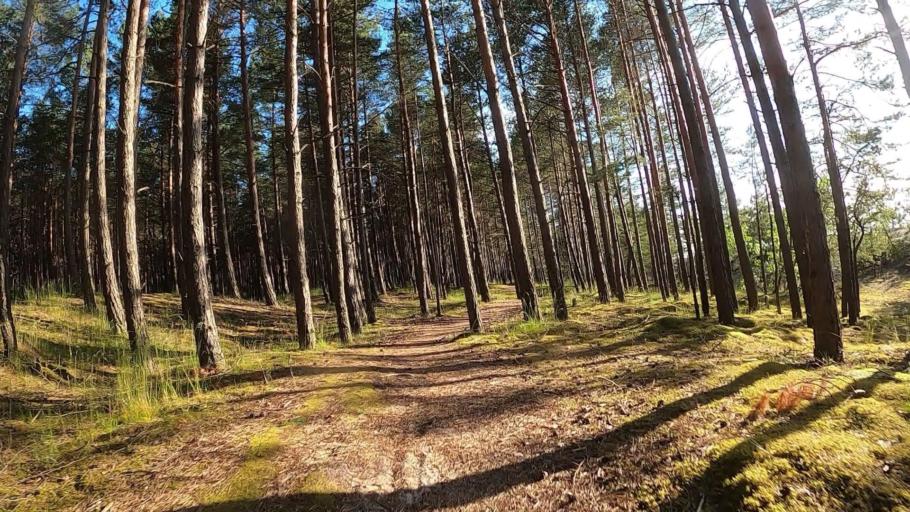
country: LV
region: Carnikava
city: Carnikava
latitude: 57.1238
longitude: 24.2113
